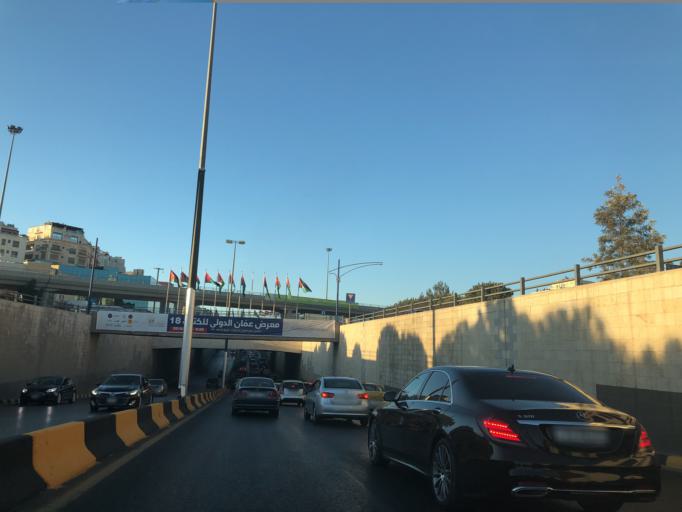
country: JO
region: Amman
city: Wadi as Sir
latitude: 31.9932
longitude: 35.8305
